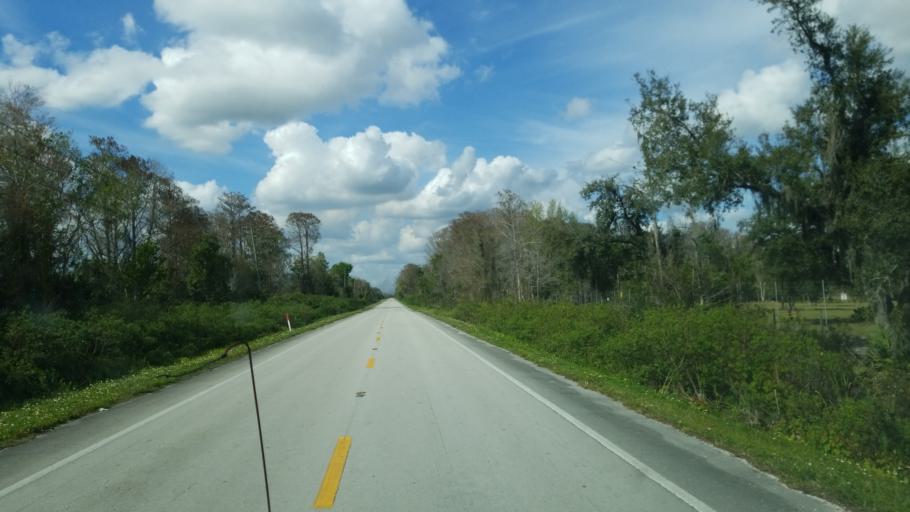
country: US
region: Florida
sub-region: Brevard County
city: June Park
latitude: 28.0047
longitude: -81.0233
